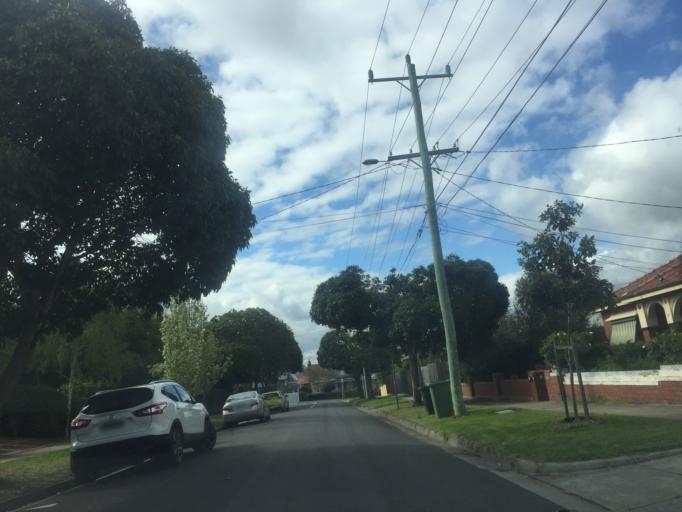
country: AU
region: Victoria
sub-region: Darebin
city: Reservoir
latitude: -37.7297
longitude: 145.0151
